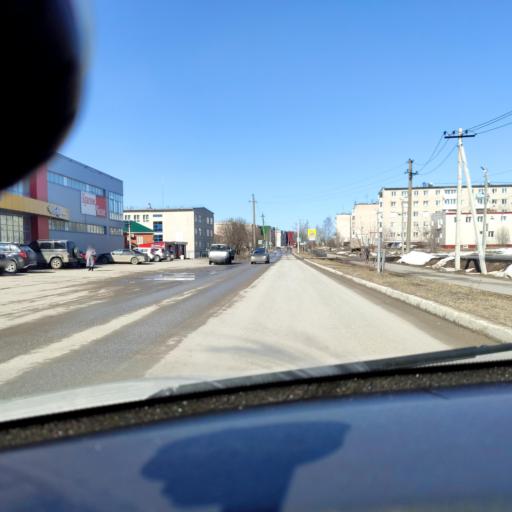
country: RU
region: Perm
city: Polazna
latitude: 58.2919
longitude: 56.3962
